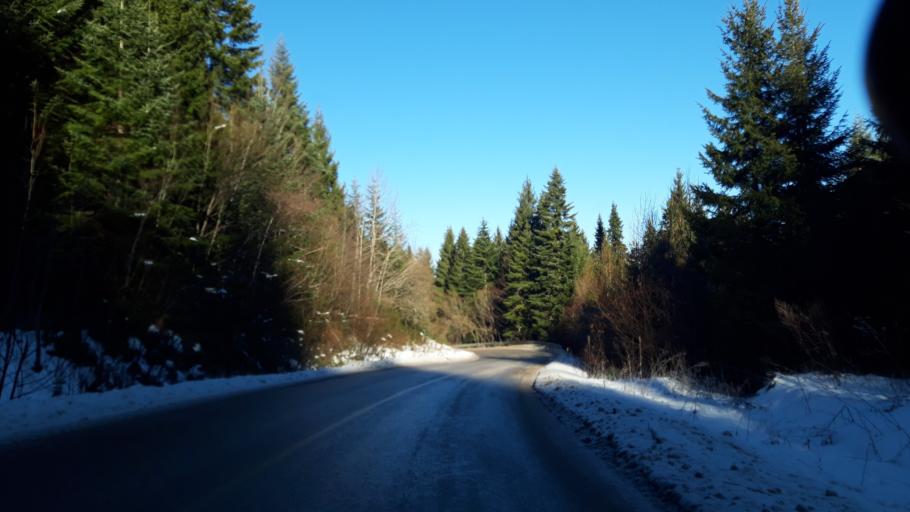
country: BA
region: Republika Srpska
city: Koran
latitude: 43.7981
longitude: 18.5516
